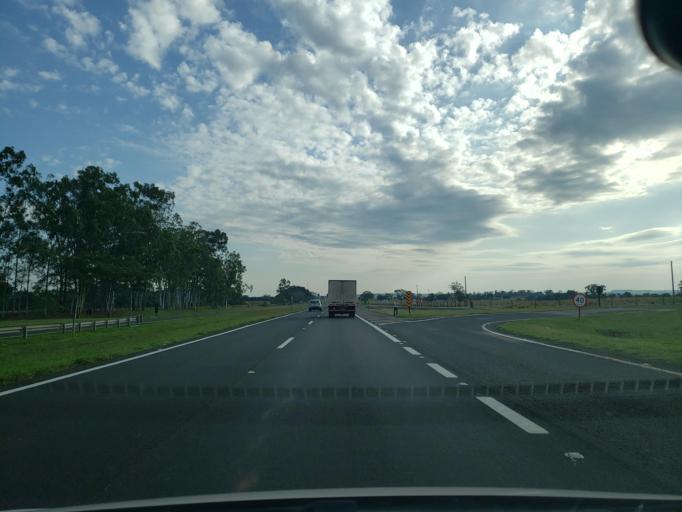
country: BR
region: Sao Paulo
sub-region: Guararapes
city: Guararapes
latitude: -21.2042
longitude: -50.6165
